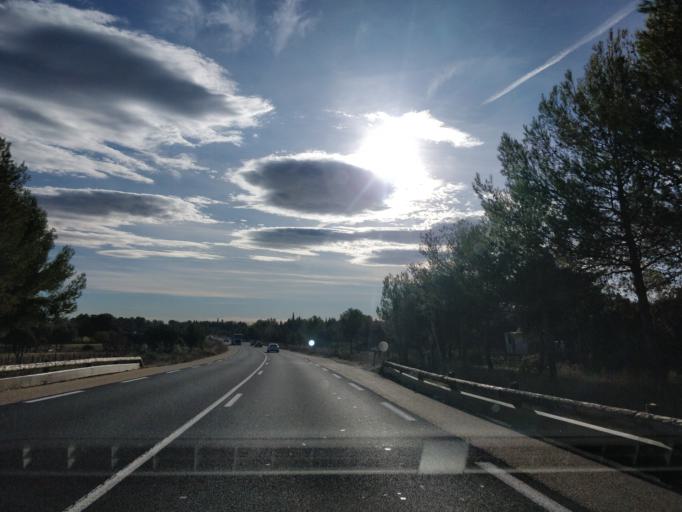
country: FR
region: Languedoc-Roussillon
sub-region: Departement de l'Herault
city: Teyran
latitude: 43.6780
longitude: 3.9483
